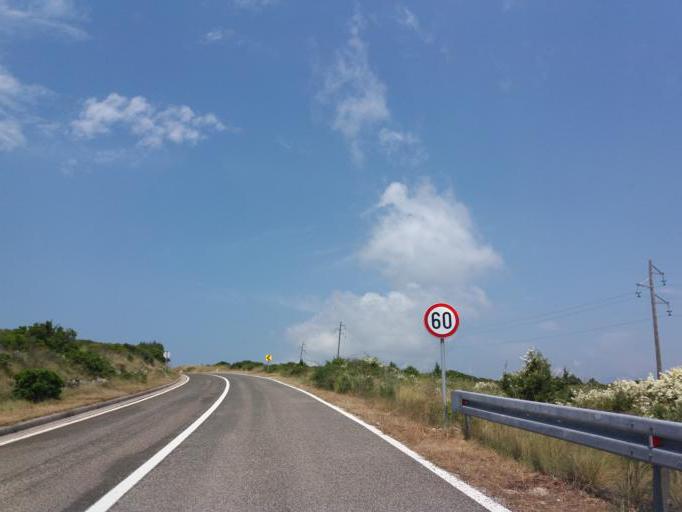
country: HR
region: Zadarska
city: Ugljan
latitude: 44.0258
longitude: 15.0318
